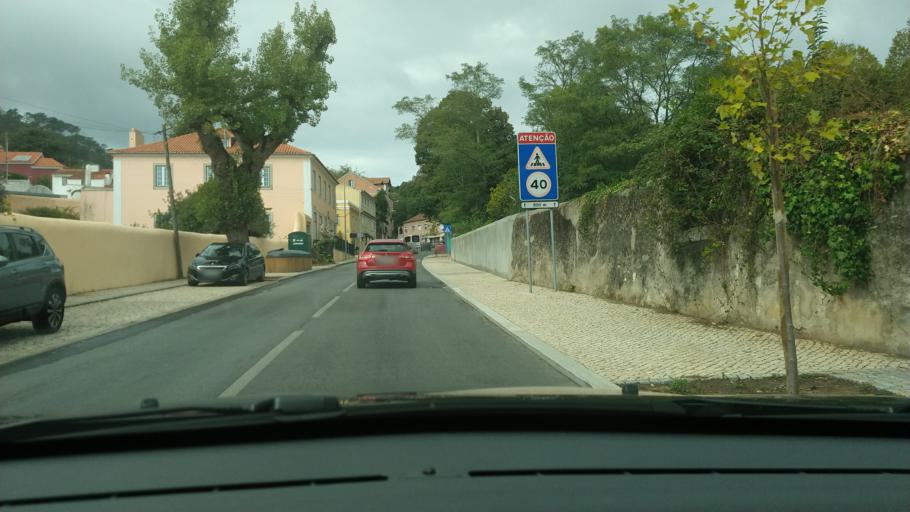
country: PT
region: Lisbon
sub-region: Sintra
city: Sintra
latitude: 38.7899
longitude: -9.3765
